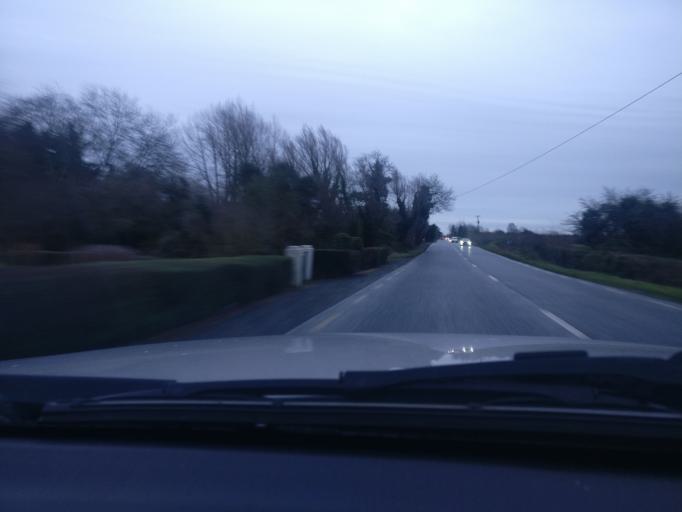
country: IE
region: Leinster
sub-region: An Mhi
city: Navan
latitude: 53.6771
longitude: -6.7491
